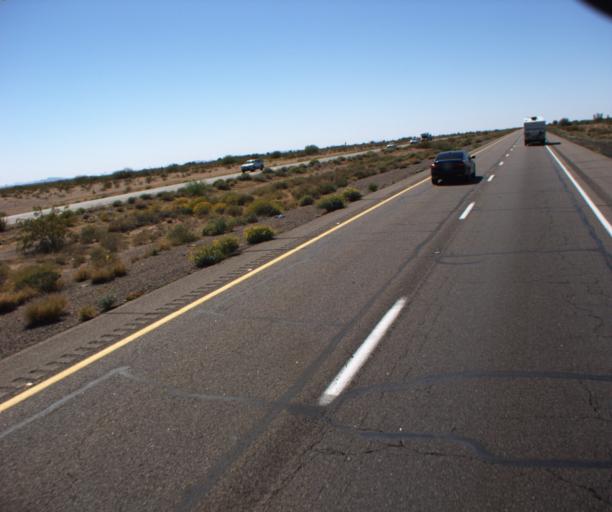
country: US
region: Arizona
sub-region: Maricopa County
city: Gila Bend
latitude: 32.9004
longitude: -113.0106
